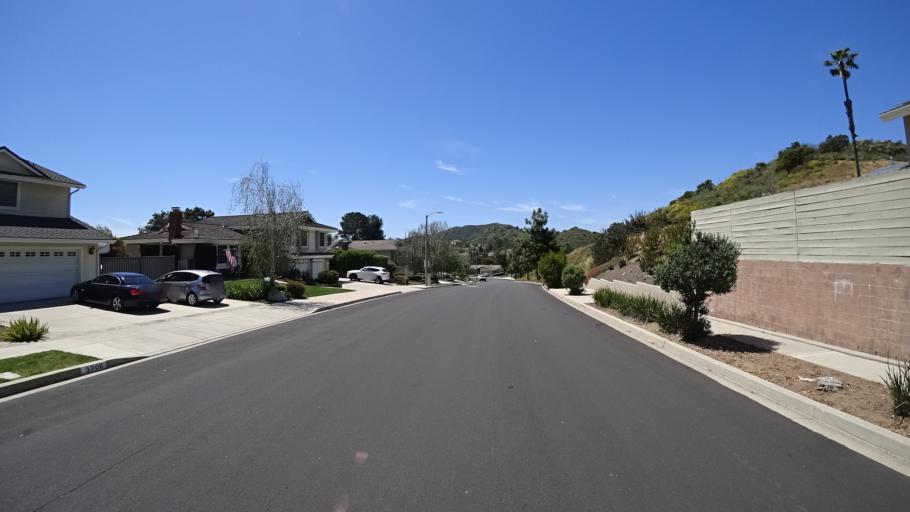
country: US
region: California
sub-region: Ventura County
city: Casa Conejo
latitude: 34.1641
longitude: -118.9530
